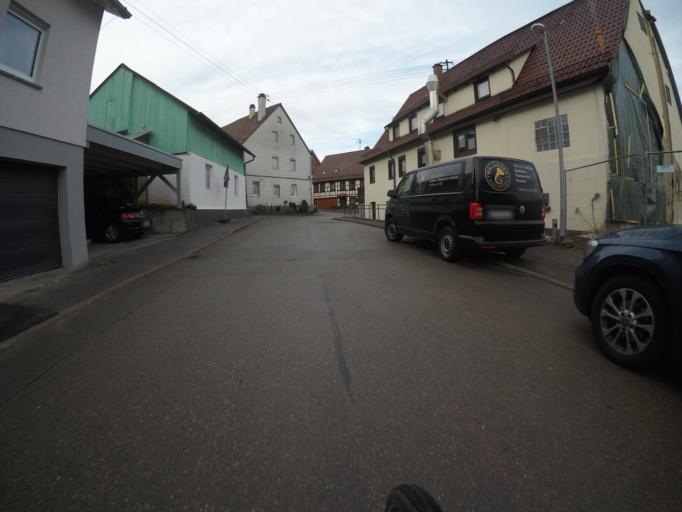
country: DE
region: Baden-Wuerttemberg
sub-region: Regierungsbezirk Stuttgart
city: Aidlingen
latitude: 48.6778
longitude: 8.8935
